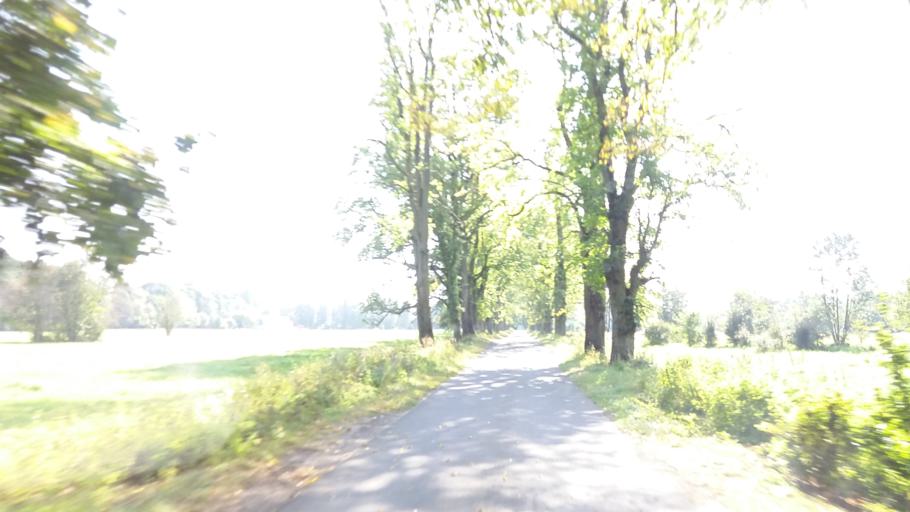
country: PL
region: West Pomeranian Voivodeship
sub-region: Powiat walecki
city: Czlopa
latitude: 53.0517
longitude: 15.9421
